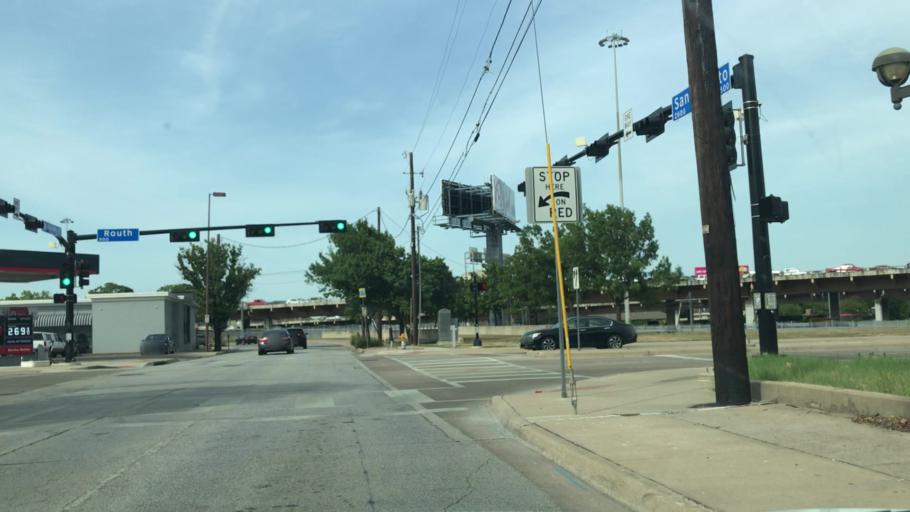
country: US
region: Texas
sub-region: Dallas County
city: Dallas
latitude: 32.7896
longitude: -96.7941
